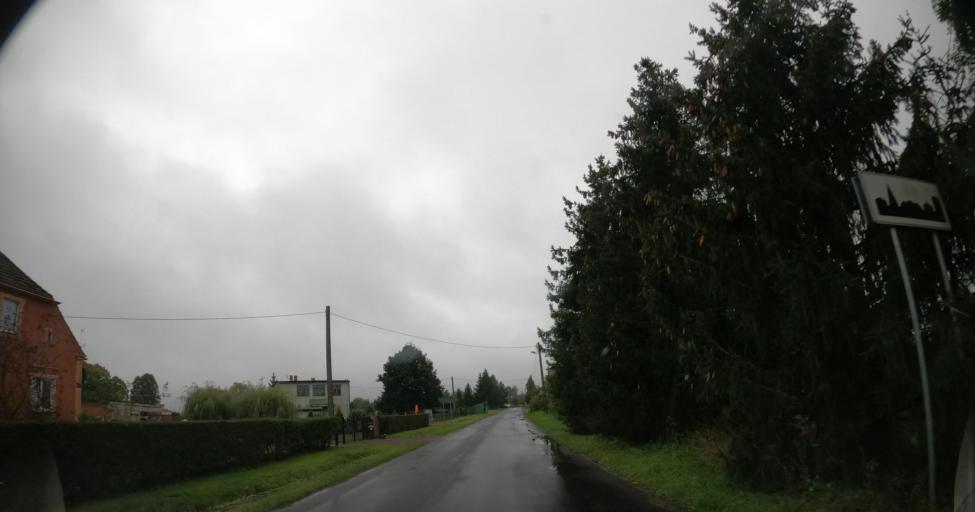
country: PL
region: West Pomeranian Voivodeship
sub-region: Powiat pyrzycki
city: Kozielice
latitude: 53.0511
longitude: 14.7752
